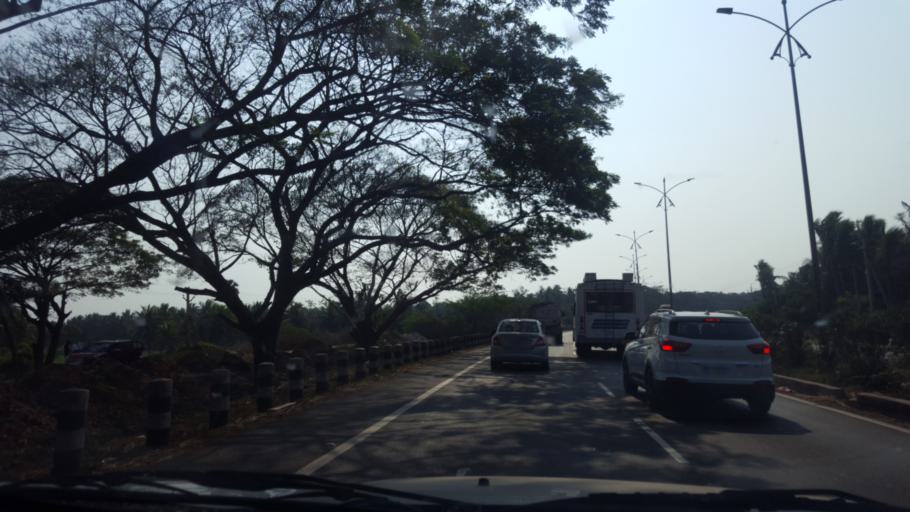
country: IN
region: Andhra Pradesh
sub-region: Vishakhapatnam
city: Anakapalle
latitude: 17.6777
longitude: 83.0244
